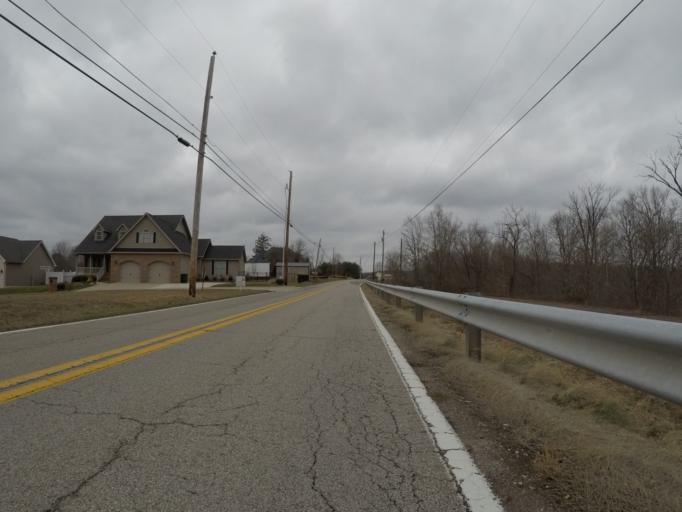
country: US
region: West Virginia
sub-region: Cabell County
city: Barboursville
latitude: 38.4271
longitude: -82.2397
